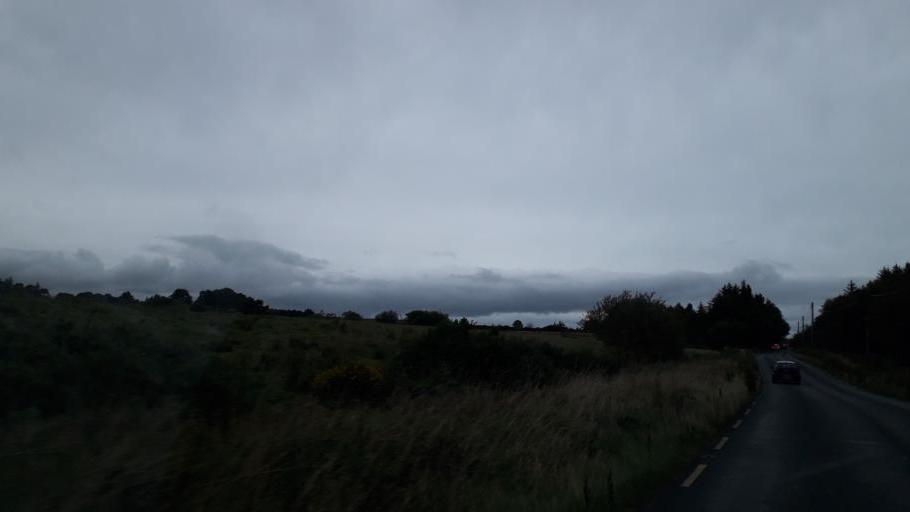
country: IE
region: Leinster
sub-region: Wicklow
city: Kilmacanoge
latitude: 53.1225
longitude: -6.1839
